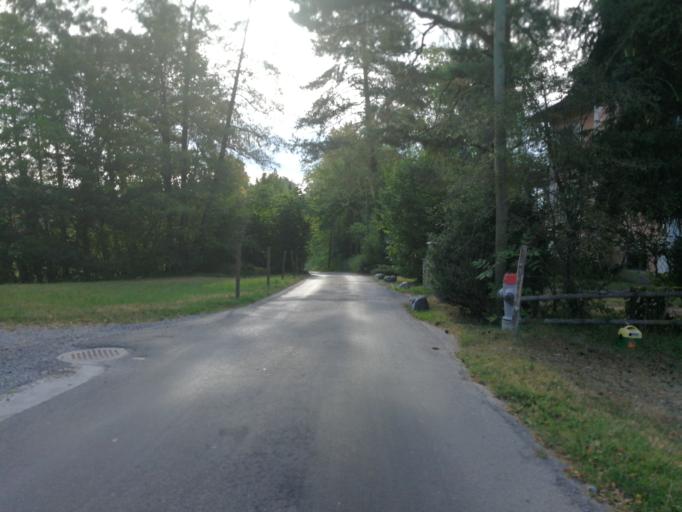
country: CH
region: Zurich
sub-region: Bezirk Meilen
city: Dorf
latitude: 47.2505
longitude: 8.7382
